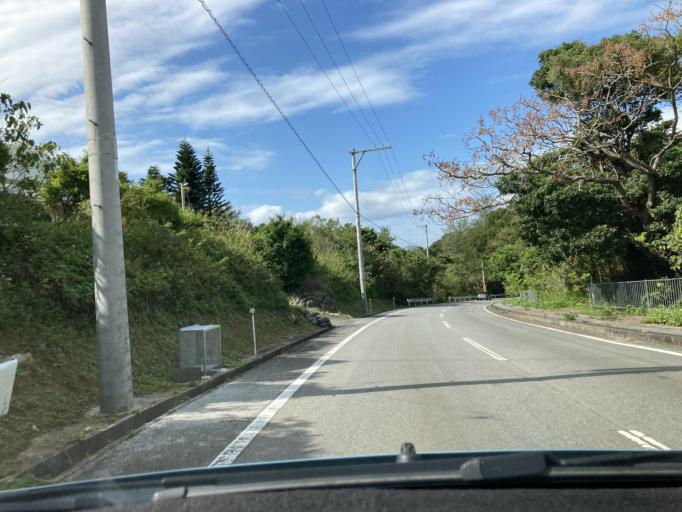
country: JP
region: Okinawa
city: Nago
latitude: 26.6923
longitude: 127.9258
